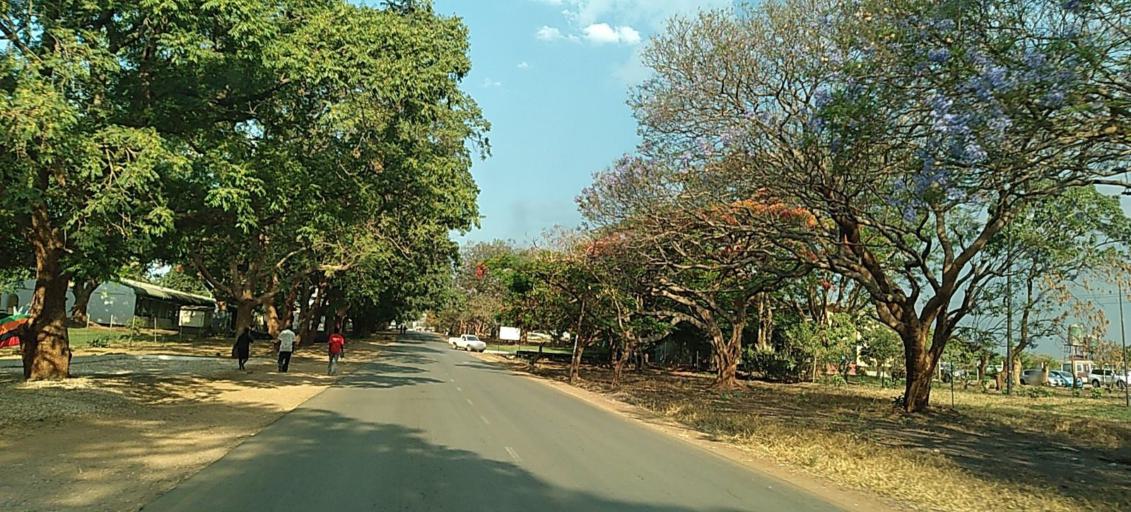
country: ZM
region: Lusaka
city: Lusaka
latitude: -15.5447
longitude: 28.2607
